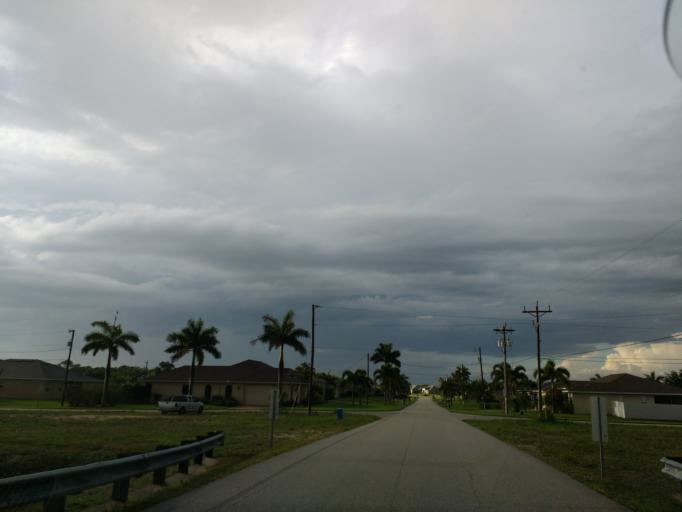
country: US
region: Florida
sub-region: Lee County
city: Cape Coral
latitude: 26.5968
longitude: -82.0234
